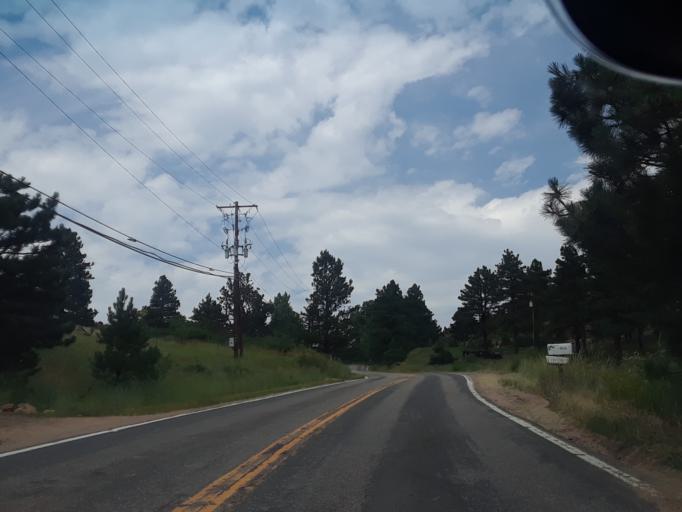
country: US
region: Colorado
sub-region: Boulder County
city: Boulder
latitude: 40.0707
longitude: -105.3016
